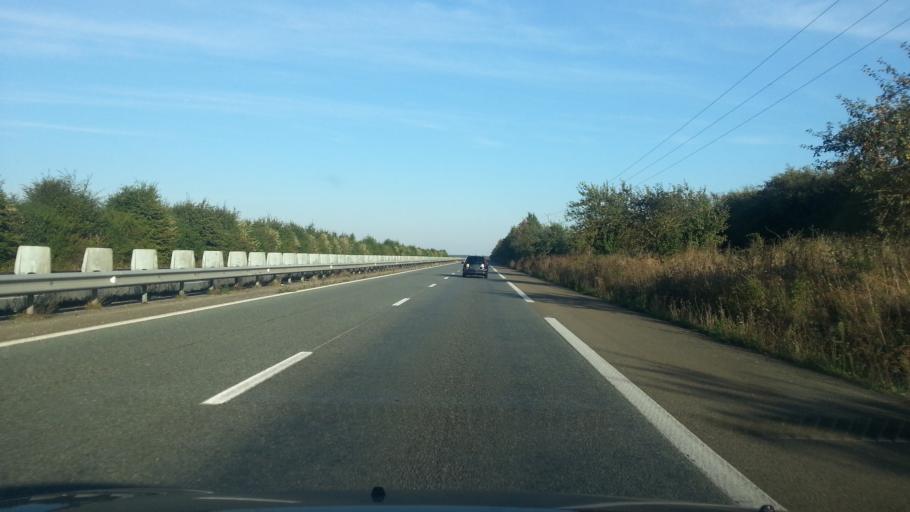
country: FR
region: Picardie
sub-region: Departement de l'Oise
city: Bresles
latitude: 49.4141
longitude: 2.2721
